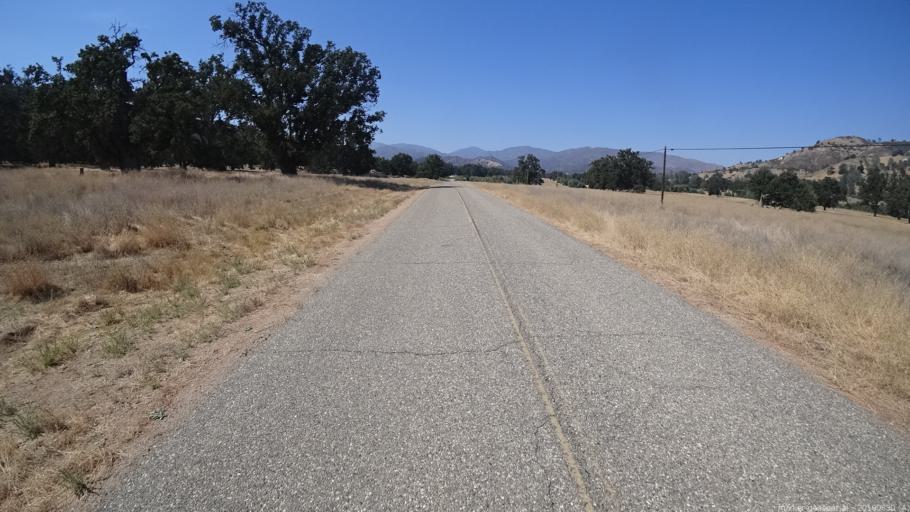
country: US
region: California
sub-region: Monterey County
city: King City
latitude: 36.0432
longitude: -121.2977
